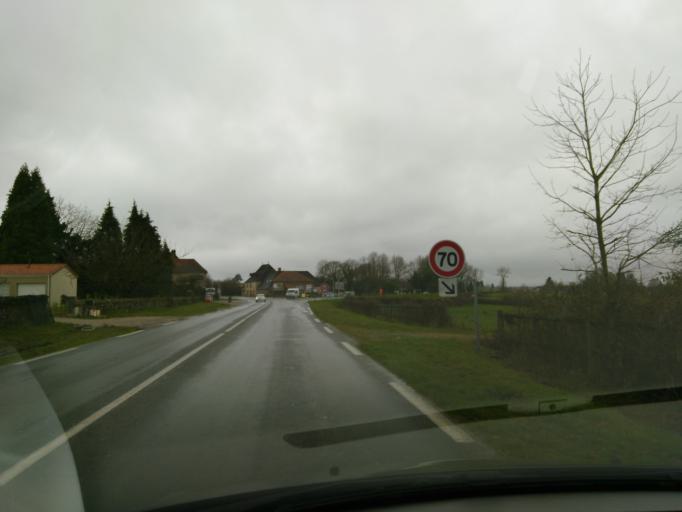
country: FR
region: Limousin
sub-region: Departement de la Haute-Vienne
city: Nexon
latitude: 45.6850
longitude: 1.2266
